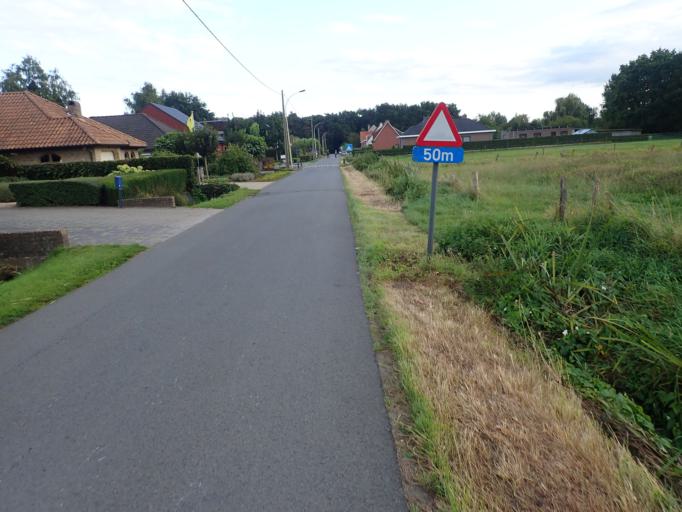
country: BE
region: Flanders
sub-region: Provincie Antwerpen
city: Zandhoven
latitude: 51.2589
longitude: 4.6525
